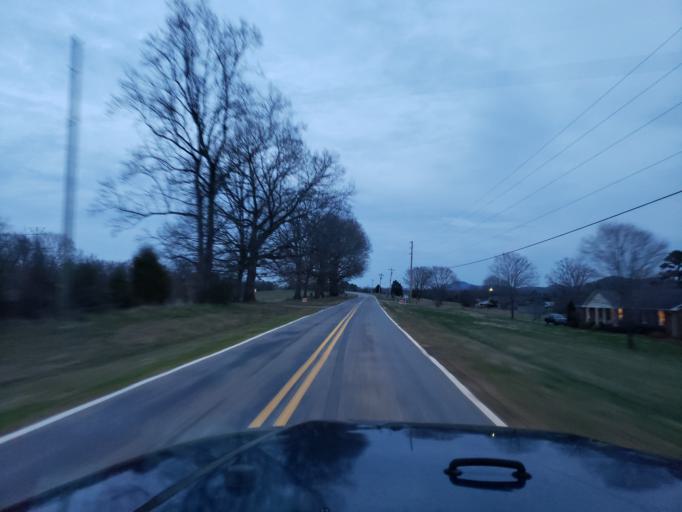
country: US
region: North Carolina
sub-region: Cleveland County
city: White Plains
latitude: 35.1754
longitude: -81.3955
